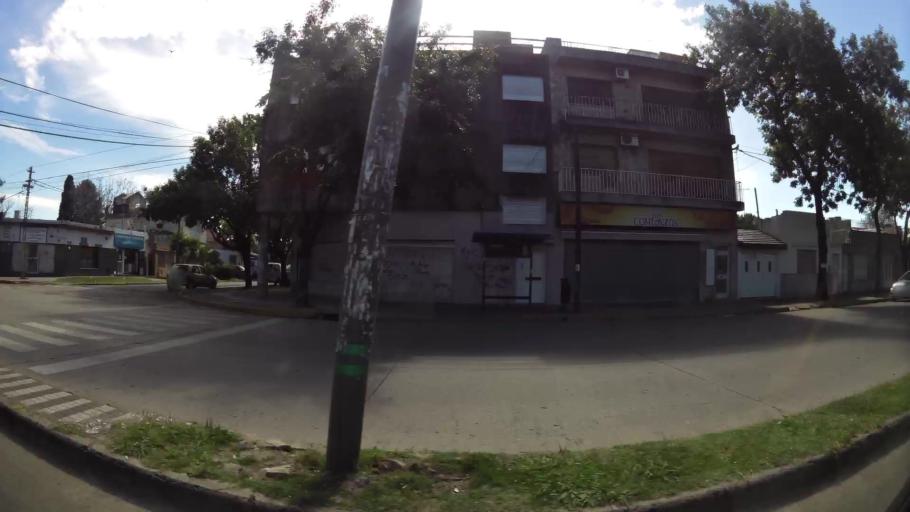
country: AR
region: Santa Fe
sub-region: Departamento de Rosario
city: Rosario
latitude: -32.9354
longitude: -60.7129
